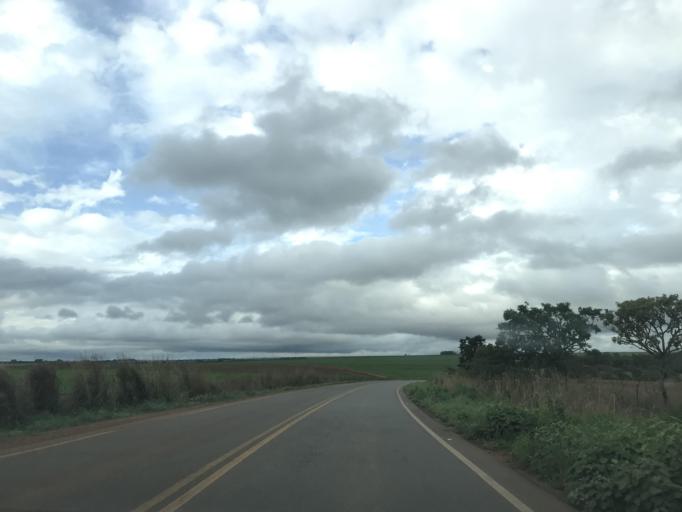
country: BR
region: Goias
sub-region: Vianopolis
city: Vianopolis
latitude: -16.5663
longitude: -48.2903
